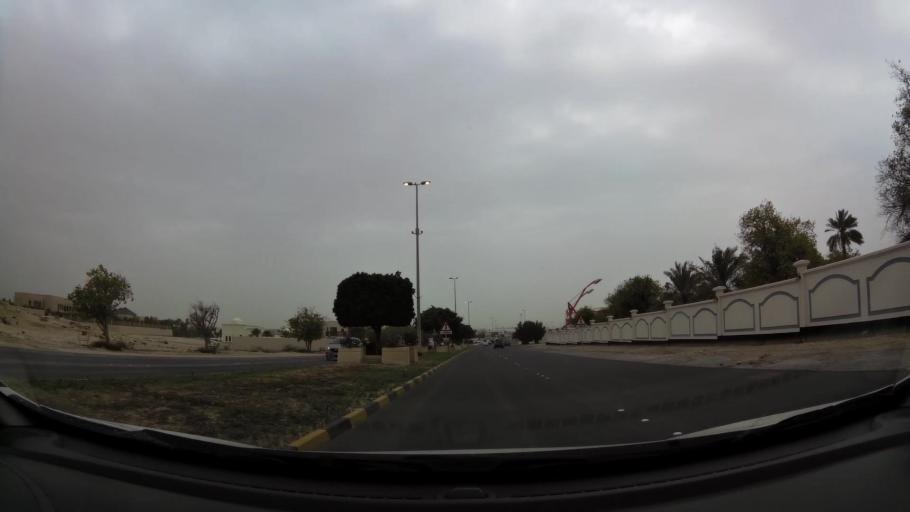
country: BH
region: Northern
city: Ar Rifa'
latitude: 26.1487
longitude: 50.5422
